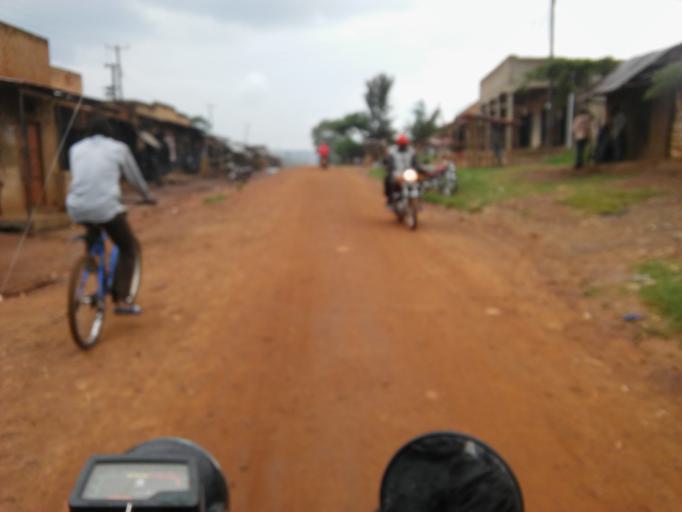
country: UG
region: Eastern Region
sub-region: Mbale District
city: Mbale
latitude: 1.0136
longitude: 34.1865
